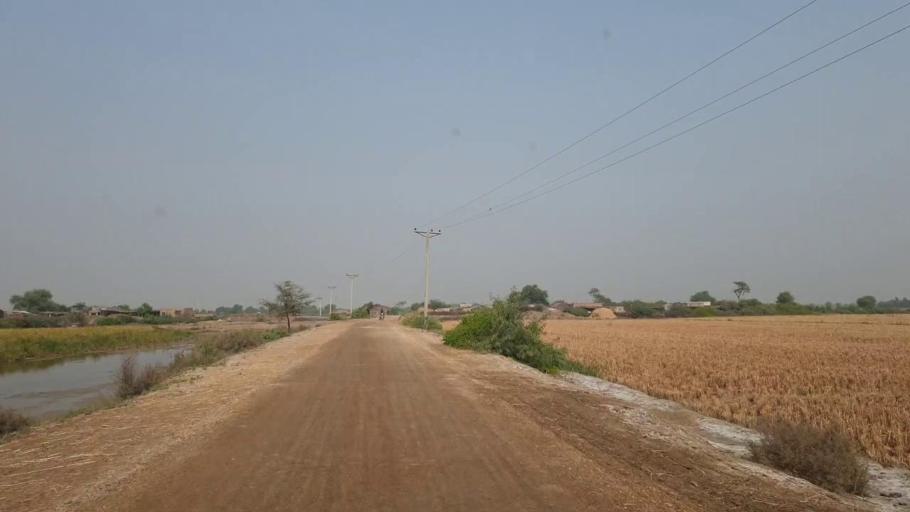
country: PK
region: Sindh
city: Matli
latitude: 25.1540
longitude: 68.7295
